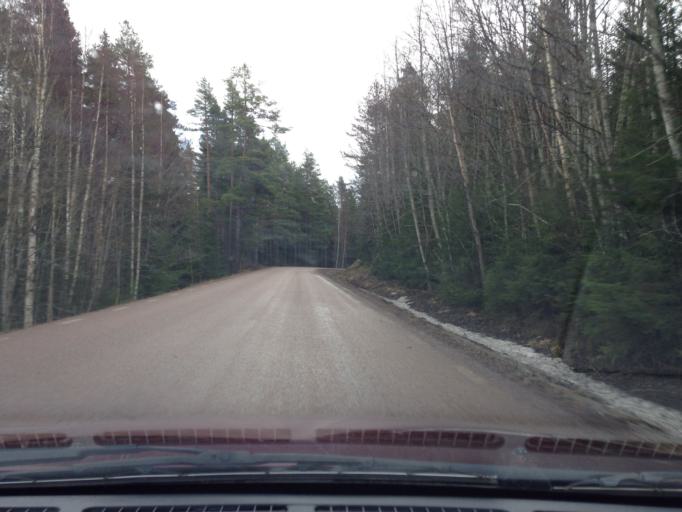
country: SE
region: Dalarna
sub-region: Ludvika Kommun
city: Ludvika
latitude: 60.1746
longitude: 15.2649
